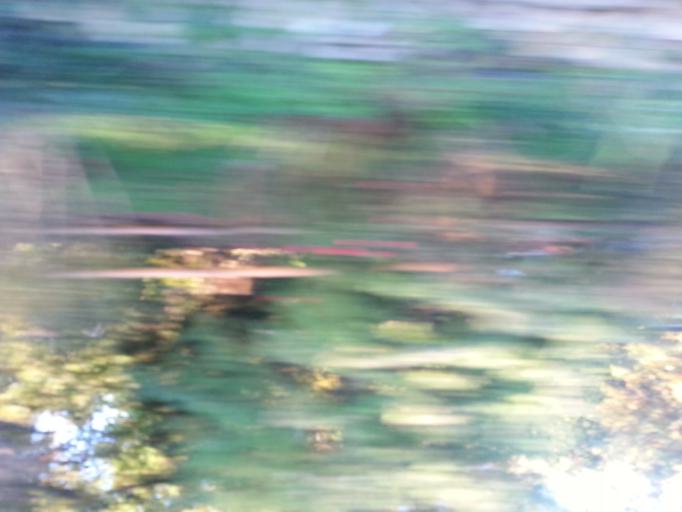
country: US
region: Tennessee
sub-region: Knox County
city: Knoxville
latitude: 36.0459
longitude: -83.9475
